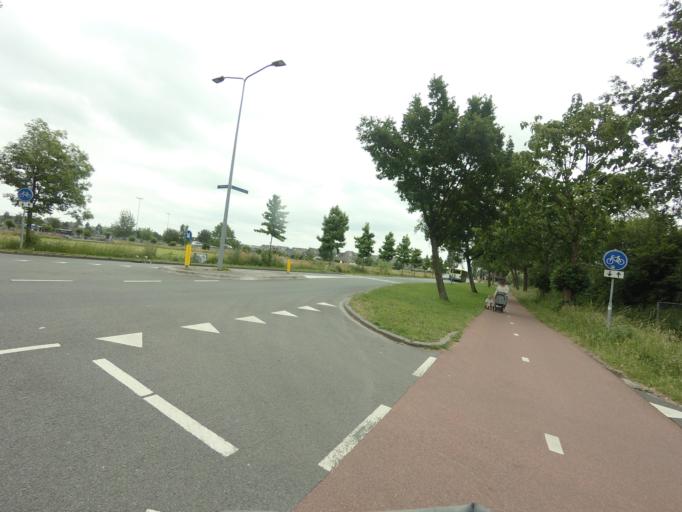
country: NL
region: North Holland
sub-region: Gemeente Huizen
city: Huizen
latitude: 52.2922
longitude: 5.2690
